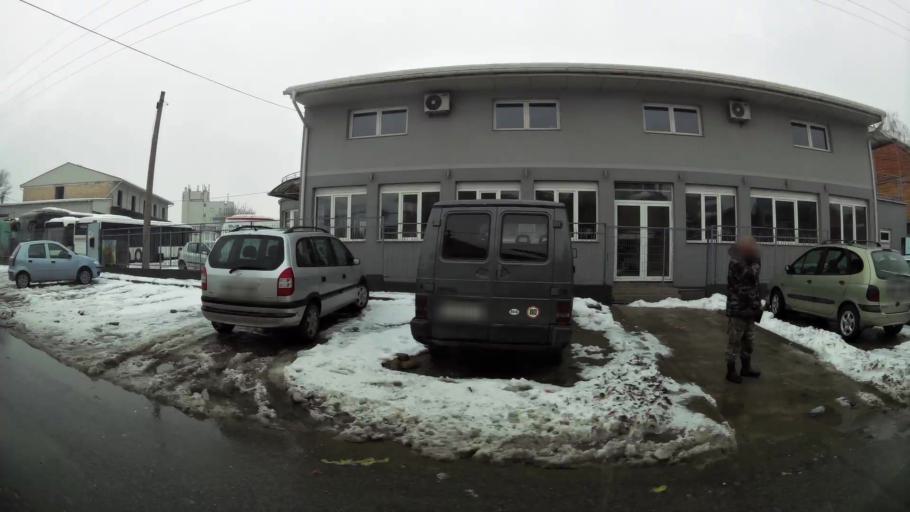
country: RS
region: Central Serbia
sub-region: Belgrade
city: Zemun
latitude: 44.8462
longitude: 20.3734
